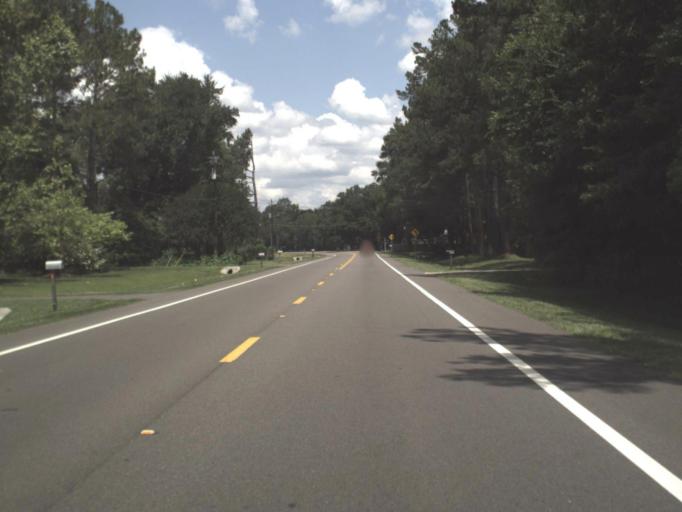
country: US
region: Florida
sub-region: Nassau County
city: Callahan
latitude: 30.5578
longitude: -81.8128
